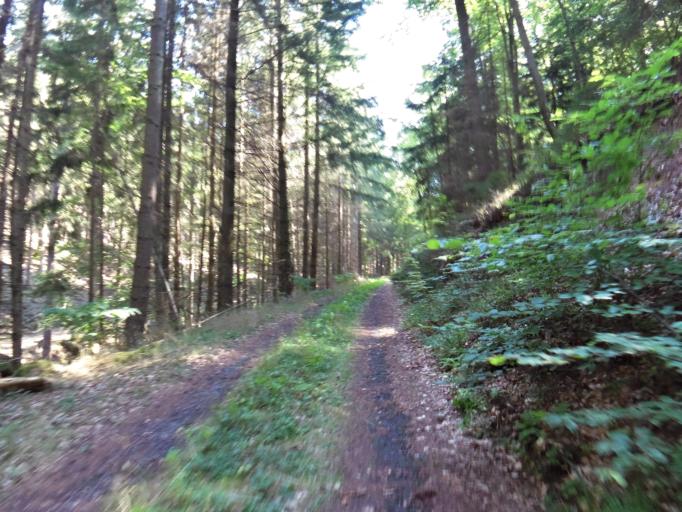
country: DE
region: Rheinland-Pfalz
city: Neidenfels
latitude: 49.4205
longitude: 8.0412
